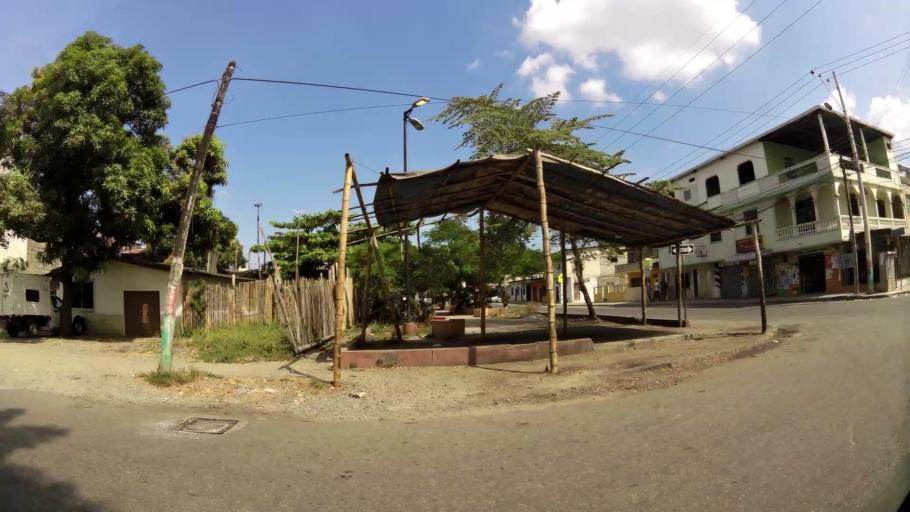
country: EC
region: Guayas
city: Guayaquil
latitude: -2.1339
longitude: -79.9383
